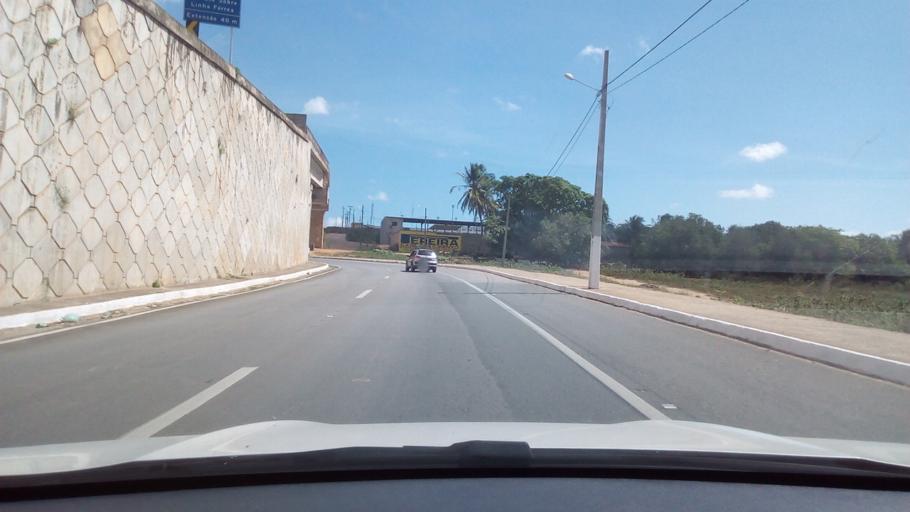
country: BR
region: Rio Grande do Norte
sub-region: Goianinha
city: Goianinha
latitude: -6.2759
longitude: -35.2071
